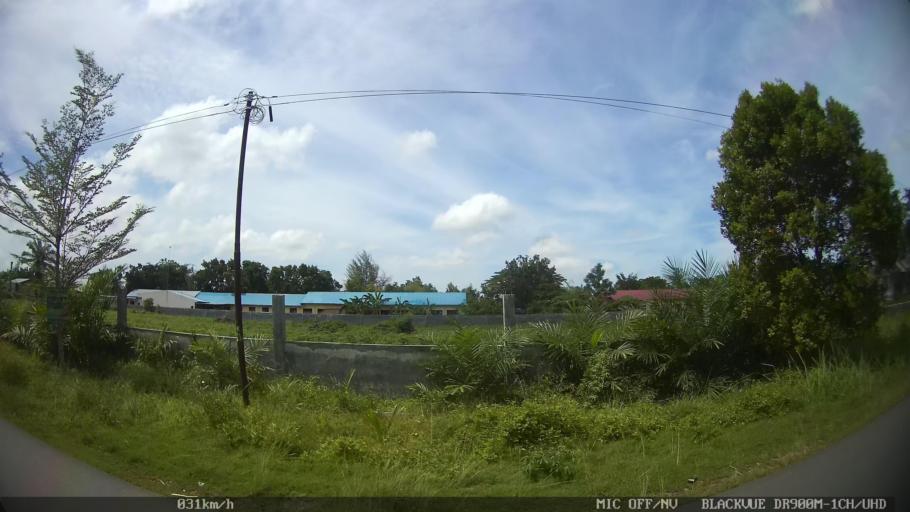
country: ID
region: North Sumatra
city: Percut
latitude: 3.5891
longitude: 98.8825
